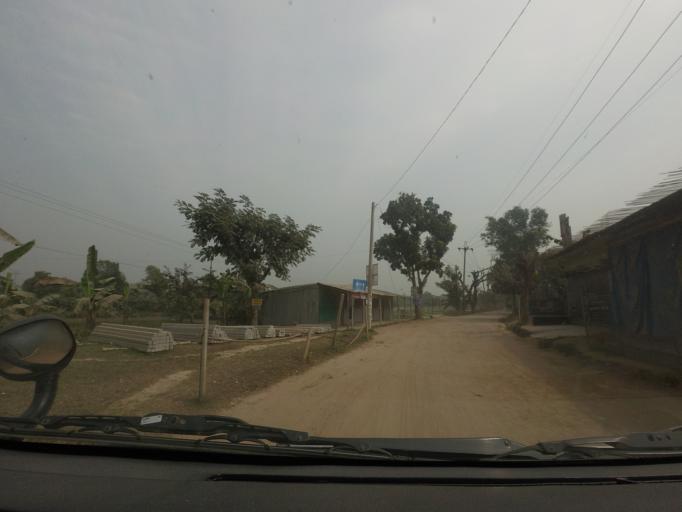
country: BD
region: Dhaka
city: Kishorganj
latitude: 24.3426
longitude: 90.7916
